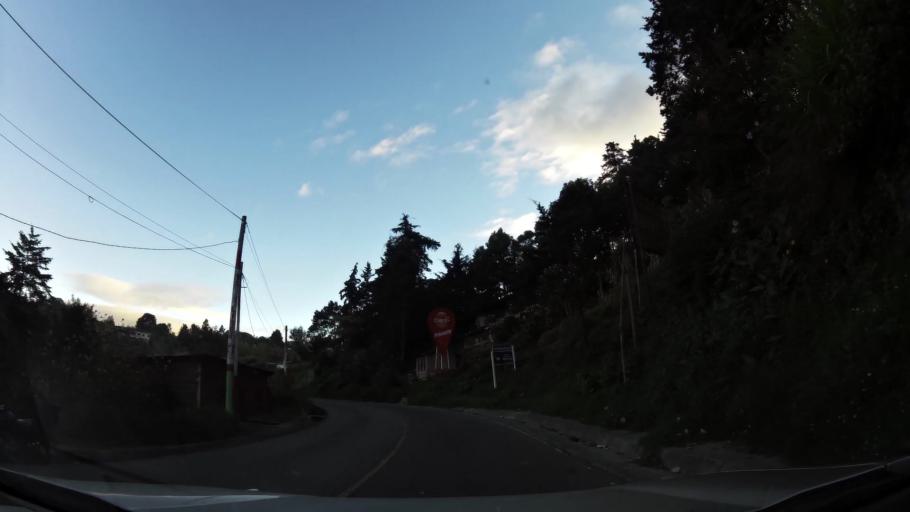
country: GT
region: Quiche
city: Chichicastenango
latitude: 14.9336
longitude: -91.1097
